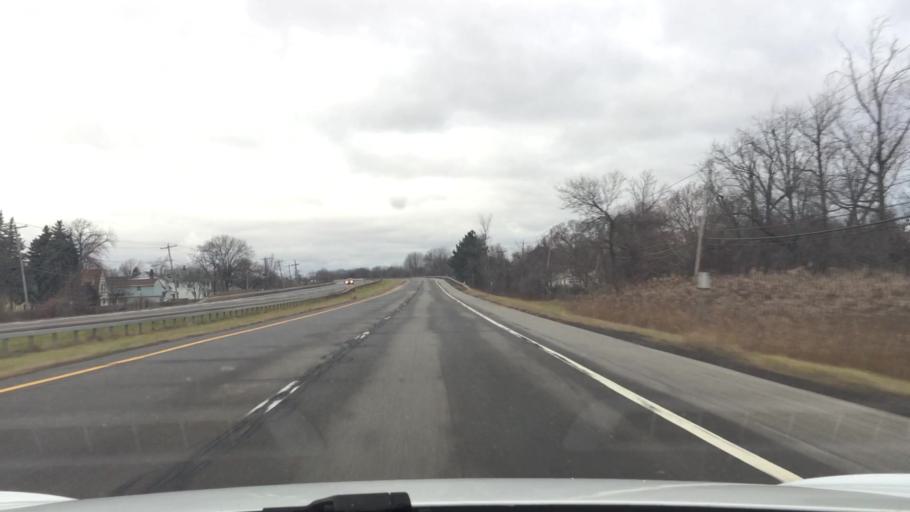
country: US
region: New York
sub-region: Erie County
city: Grandyle Village
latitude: 43.0770
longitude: -78.9533
